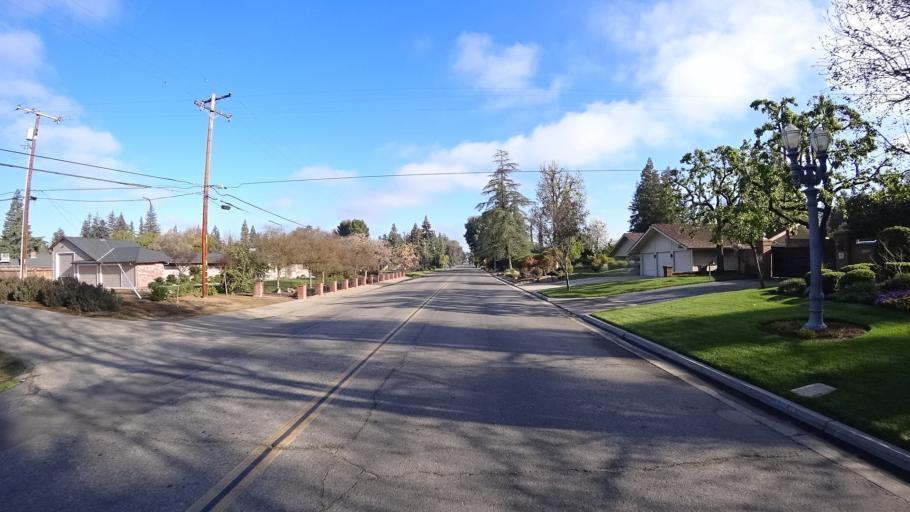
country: US
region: California
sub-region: Fresno County
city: Fresno
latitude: 36.8135
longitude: -119.8309
